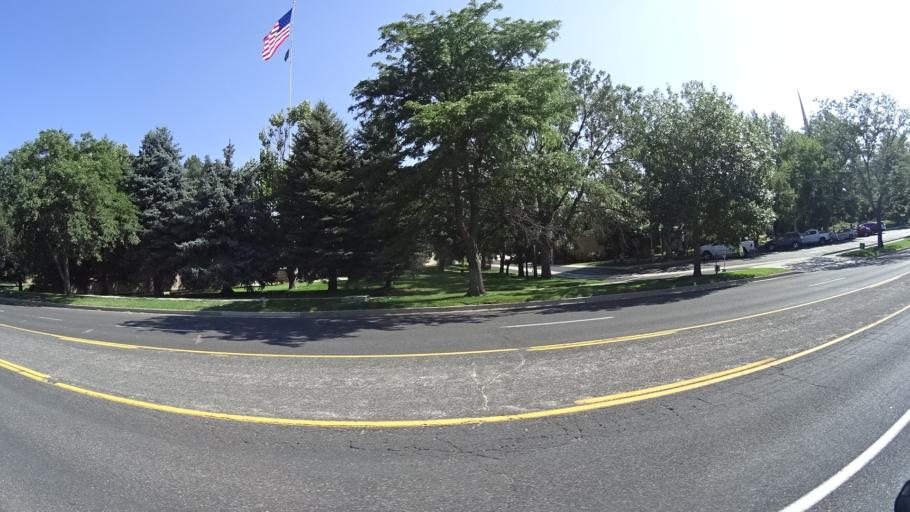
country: US
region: Colorado
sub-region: El Paso County
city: Colorado Springs
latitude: 38.8185
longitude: -104.7949
